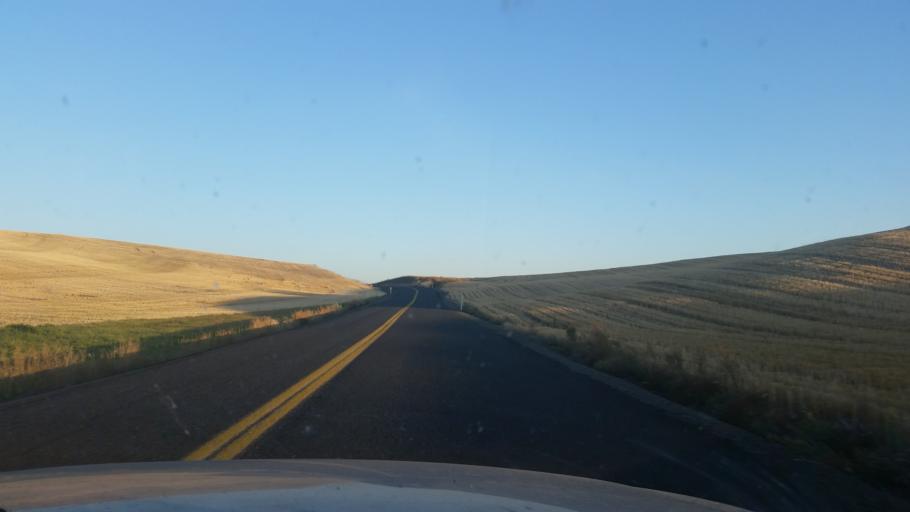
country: US
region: Washington
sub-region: Spokane County
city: Cheney
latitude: 47.5321
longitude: -117.6200
